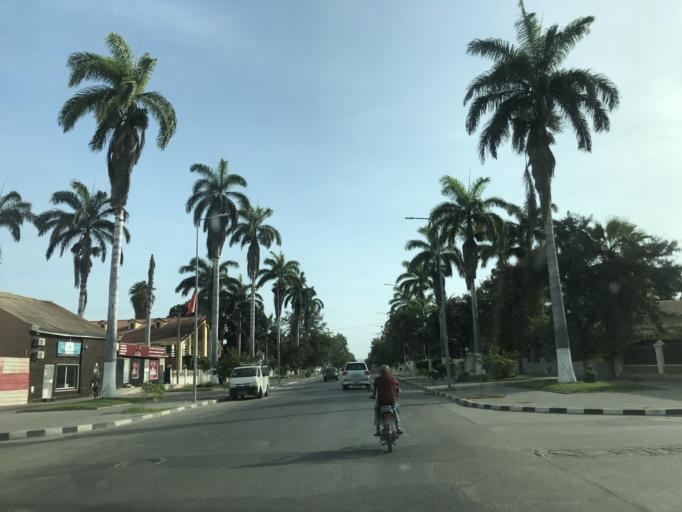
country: AO
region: Benguela
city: Benguela
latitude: -12.5766
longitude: 13.4001
